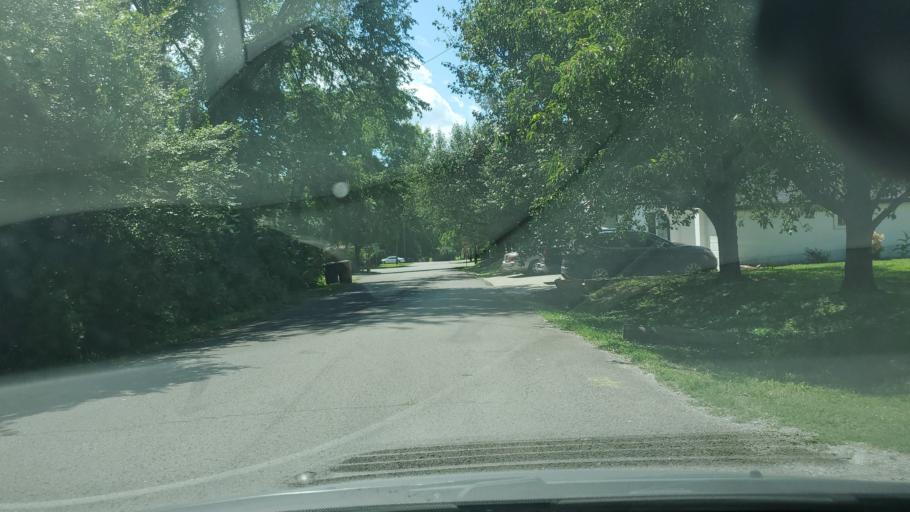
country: US
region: Tennessee
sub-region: Davidson County
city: Nashville
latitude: 36.1970
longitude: -86.7544
